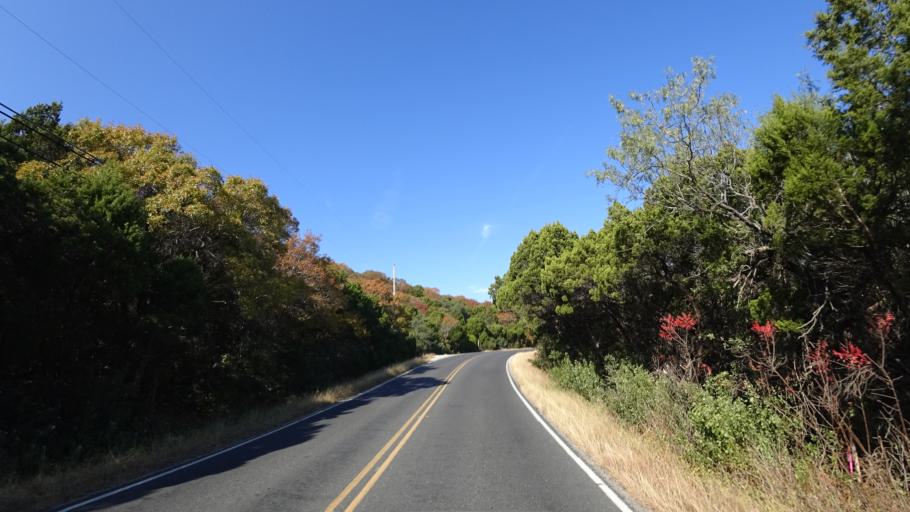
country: US
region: Texas
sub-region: Williamson County
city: Jollyville
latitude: 30.3867
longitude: -97.7726
